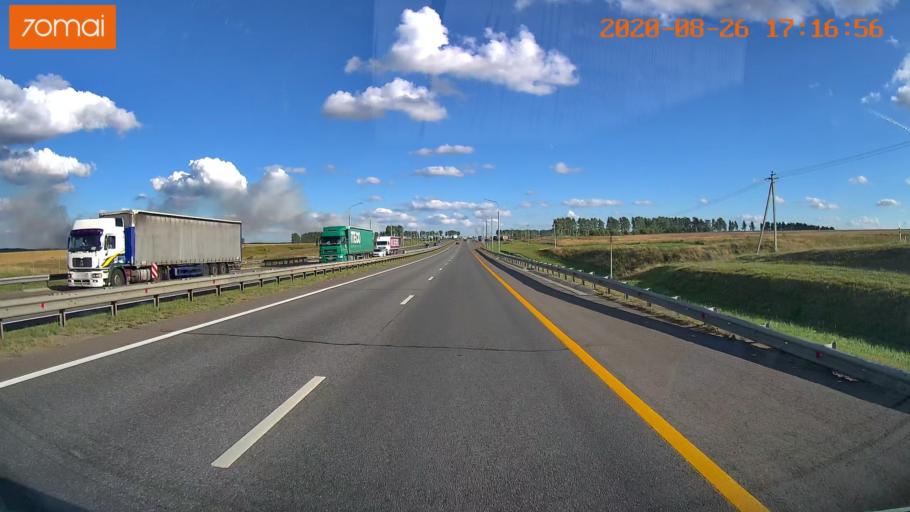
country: RU
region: Tula
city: Volovo
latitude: 53.6300
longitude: 38.0792
